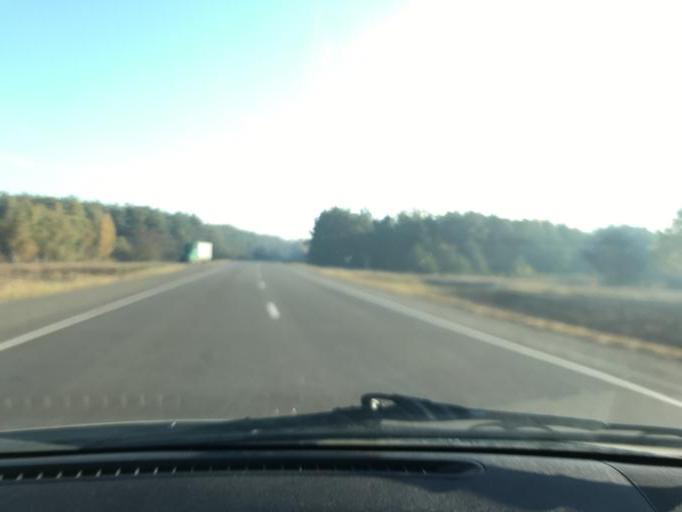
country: BY
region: Brest
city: Asnyezhytsy
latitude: 52.2928
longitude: 26.4210
